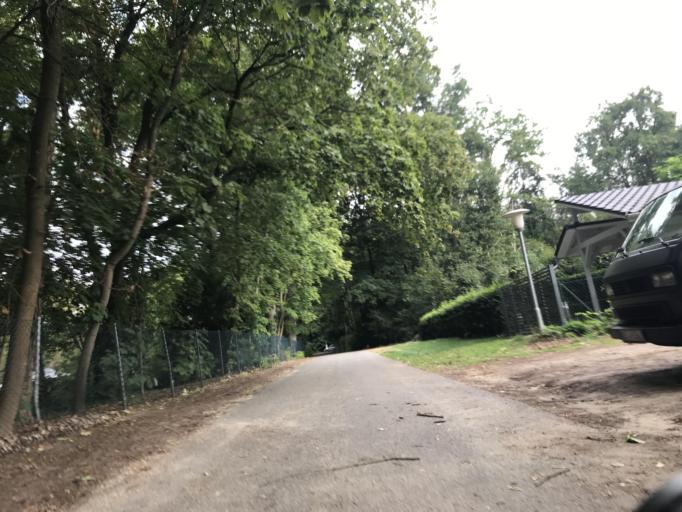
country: DE
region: Lower Saxony
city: Barendorf
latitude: 53.2278
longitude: 10.5263
